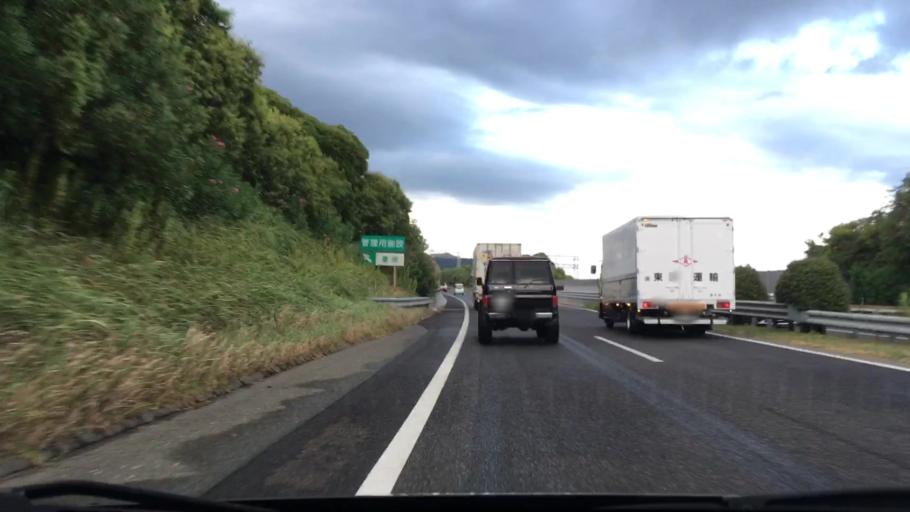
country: JP
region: Fukuoka
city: Kanda
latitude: 33.8395
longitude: 130.9262
